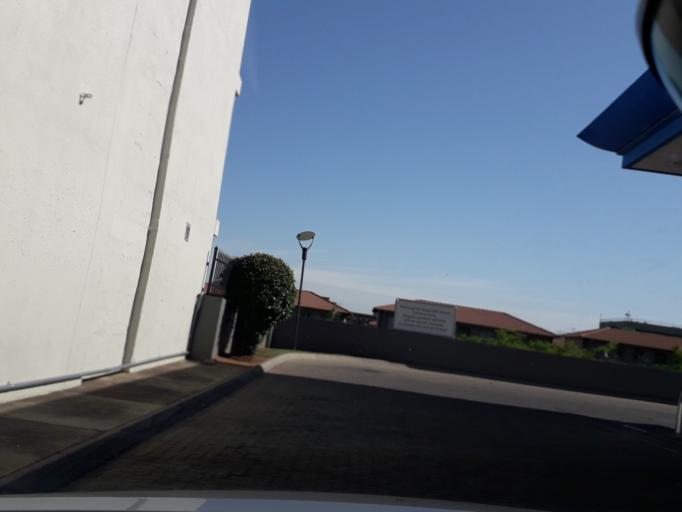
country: ZA
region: Gauteng
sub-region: City of Johannesburg Metropolitan Municipality
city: Johannesburg
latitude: -26.0924
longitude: 27.9993
